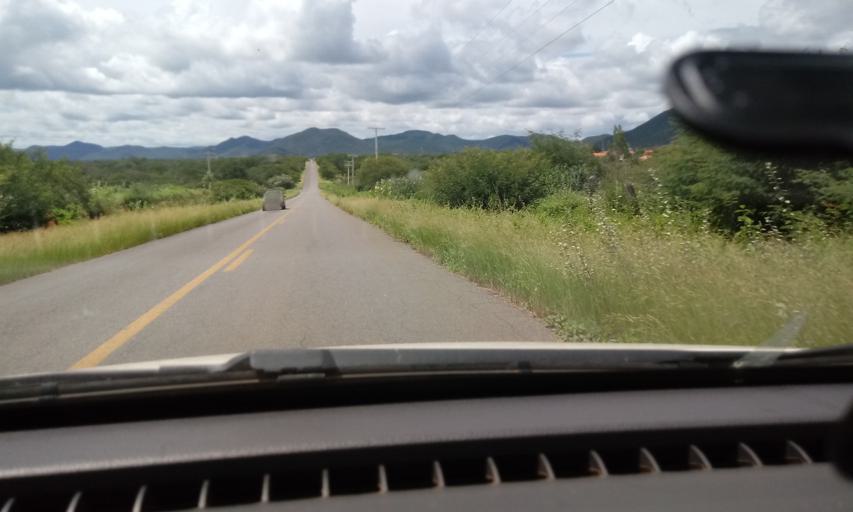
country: BR
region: Bahia
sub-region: Guanambi
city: Guanambi
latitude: -13.9332
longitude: -42.8488
